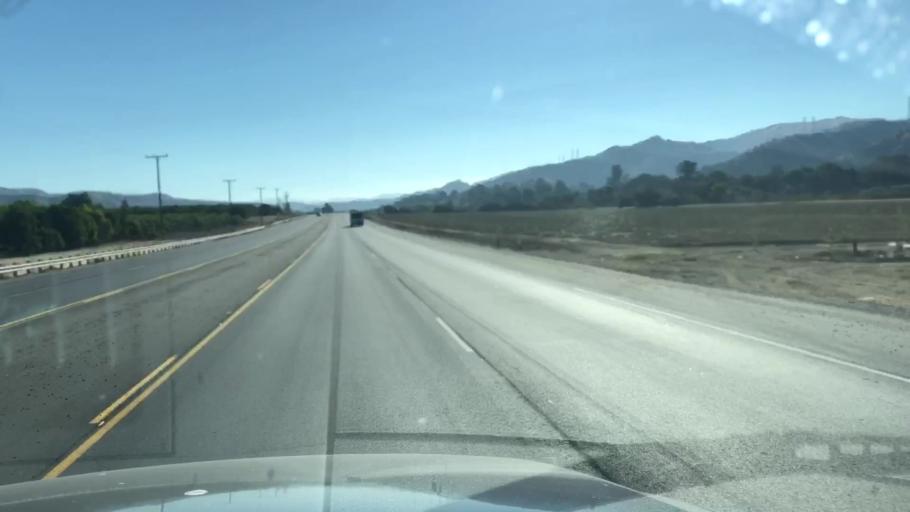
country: US
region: California
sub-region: Ventura County
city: Piru
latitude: 34.4061
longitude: -118.7502
